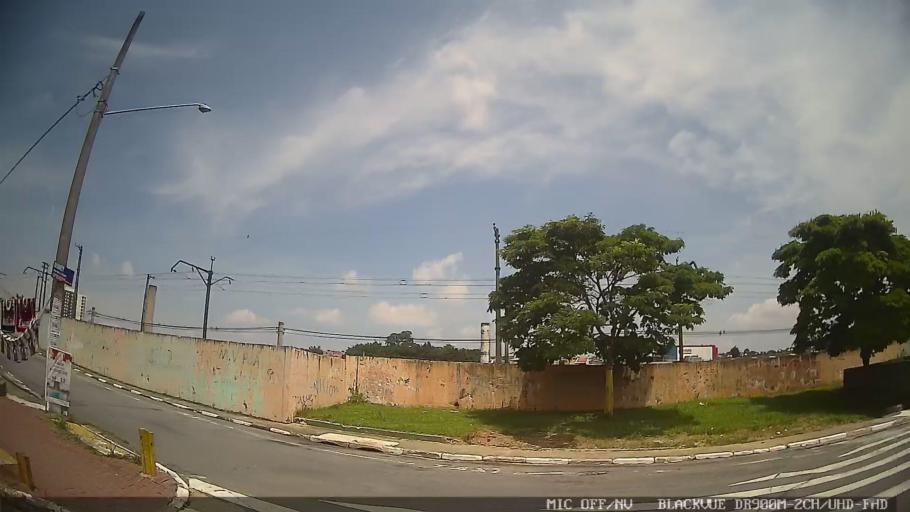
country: BR
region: Sao Paulo
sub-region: Ferraz De Vasconcelos
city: Ferraz de Vasconcelos
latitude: -23.5480
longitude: -46.3778
